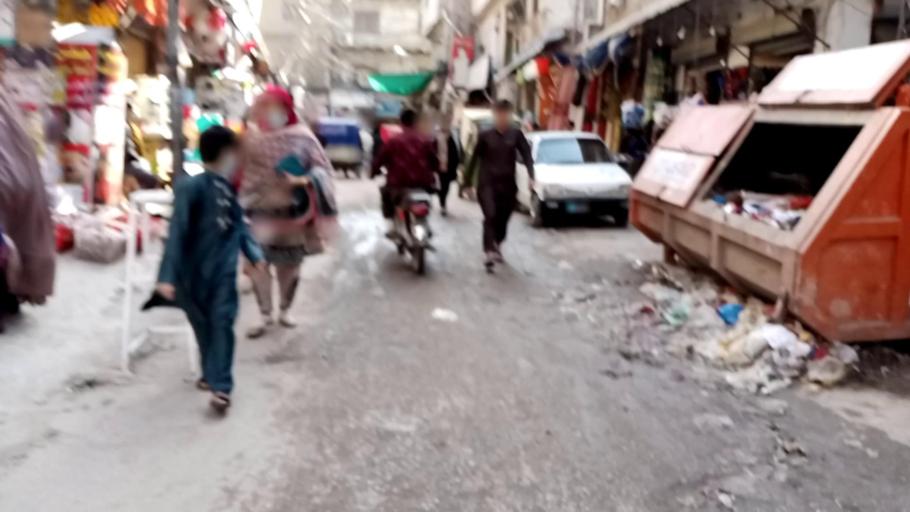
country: PK
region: Khyber Pakhtunkhwa
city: Peshawar
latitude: 34.0118
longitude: 71.5803
